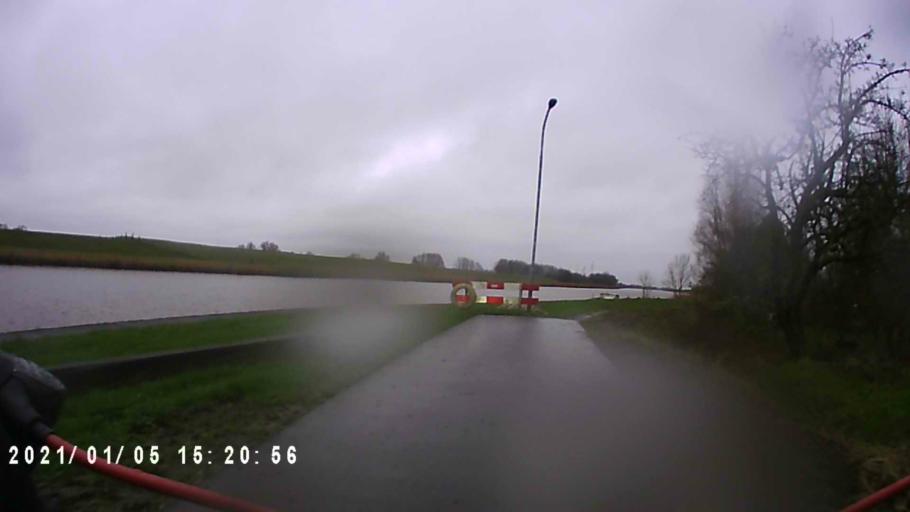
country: DE
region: Lower Saxony
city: Bunde
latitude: 53.2292
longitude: 7.2087
